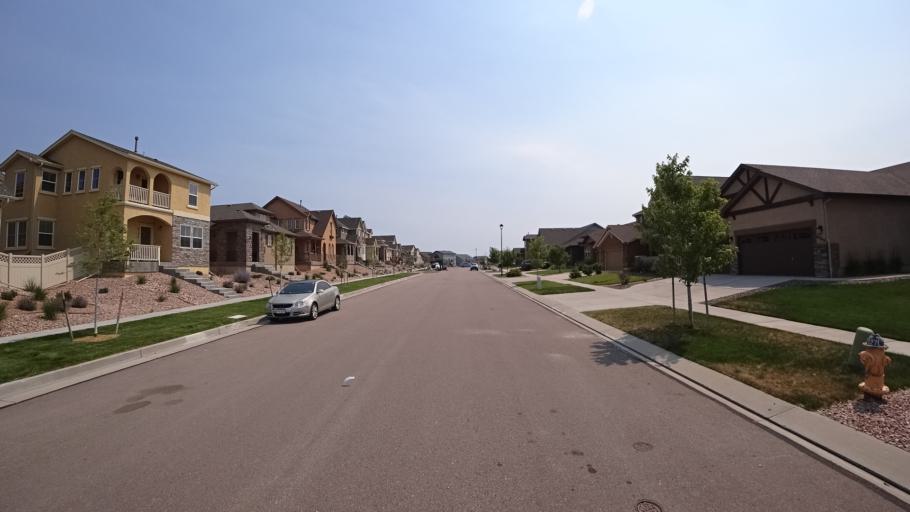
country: US
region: Colorado
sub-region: El Paso County
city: Black Forest
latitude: 38.9697
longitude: -104.7174
